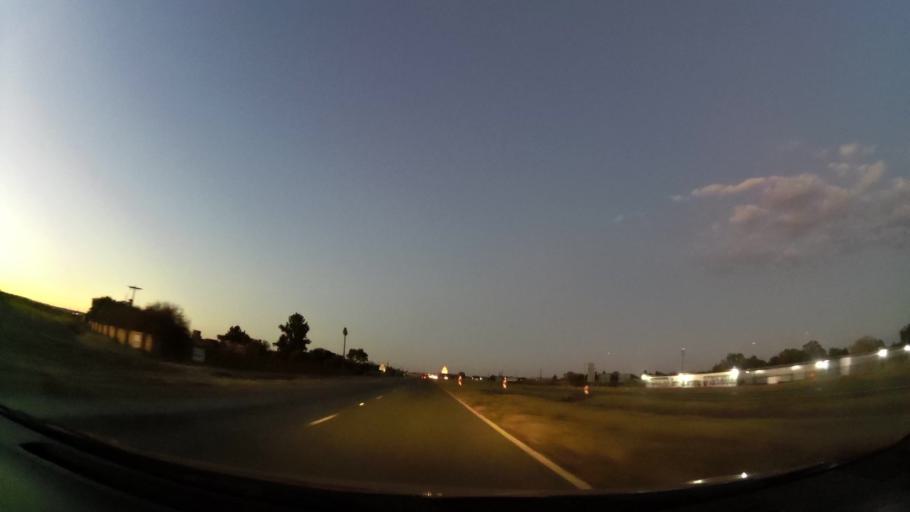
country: ZA
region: North-West
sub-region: Dr Kenneth Kaunda District Municipality
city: Potchefstroom
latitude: -26.6987
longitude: 27.1310
